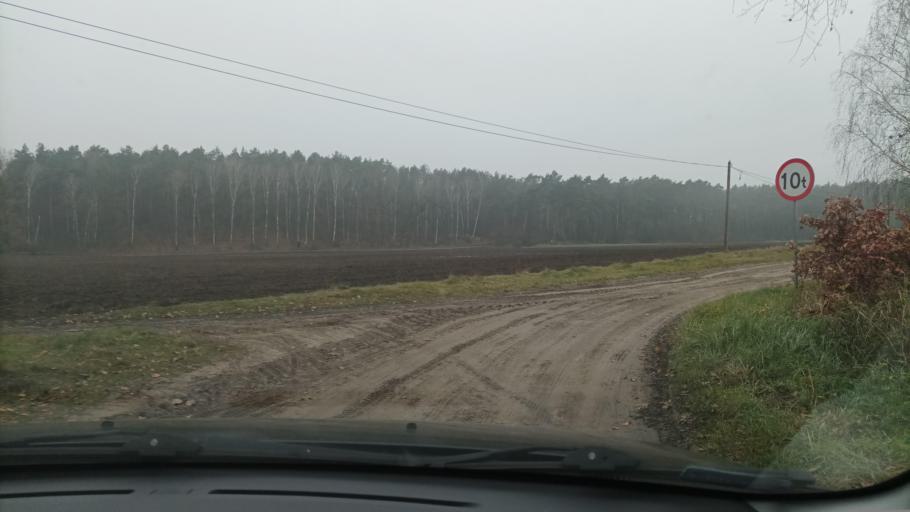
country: PL
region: Greater Poland Voivodeship
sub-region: Powiat obornicki
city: Ryczywol
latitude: 52.7525
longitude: 16.8125
